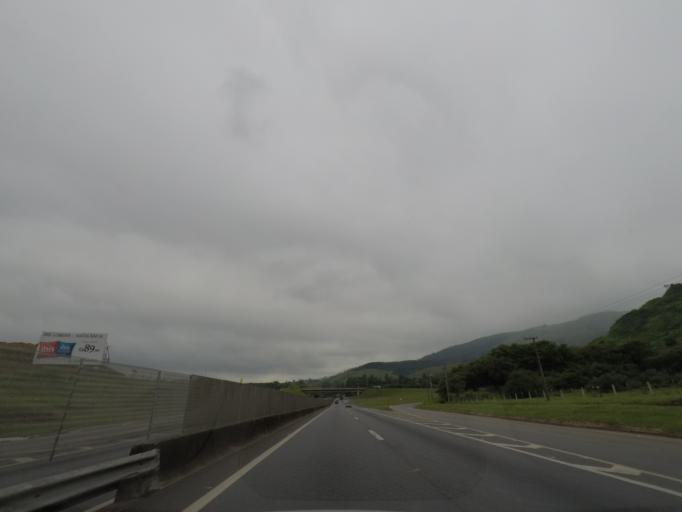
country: BR
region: Sao Paulo
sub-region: Aparecida
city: Aparecida
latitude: -22.8748
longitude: -45.2604
